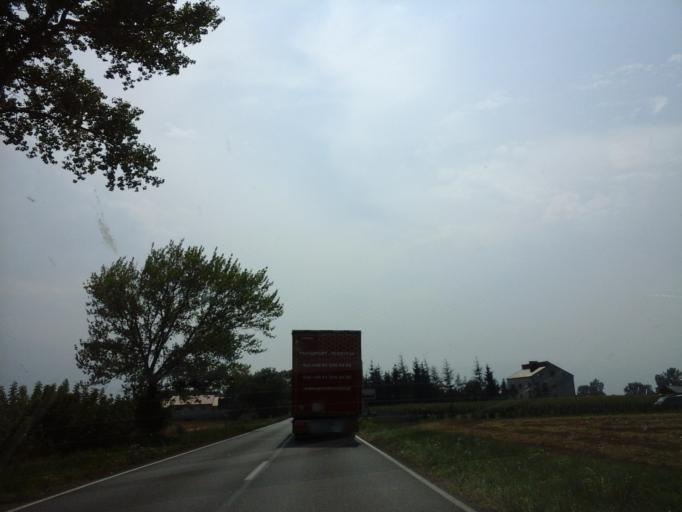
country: PL
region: Lower Silesian Voivodeship
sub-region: Powiat wroclawski
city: Zorawina
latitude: 50.9172
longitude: 17.0675
